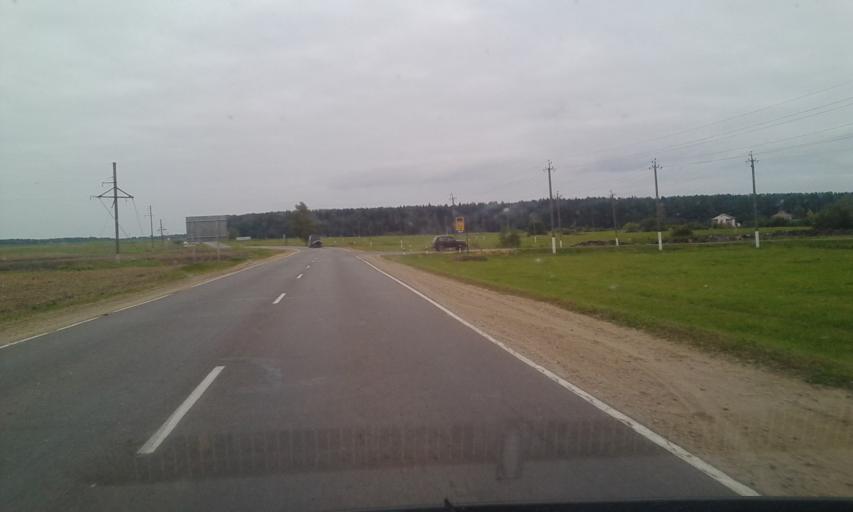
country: BY
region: Vitebsk
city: Pastavy
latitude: 55.1092
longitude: 26.8730
